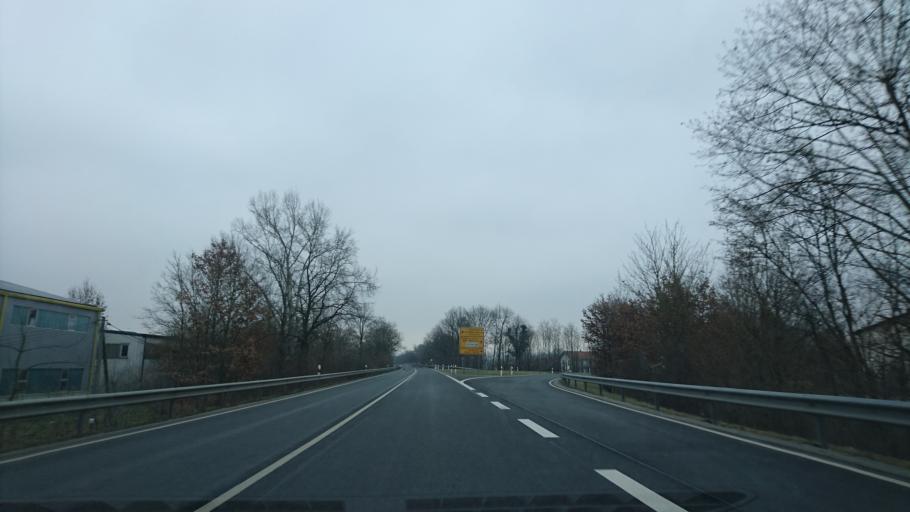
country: AT
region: Upper Austria
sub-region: Politischer Bezirk Scharding
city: Scharding
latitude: 48.4411
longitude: 13.3920
